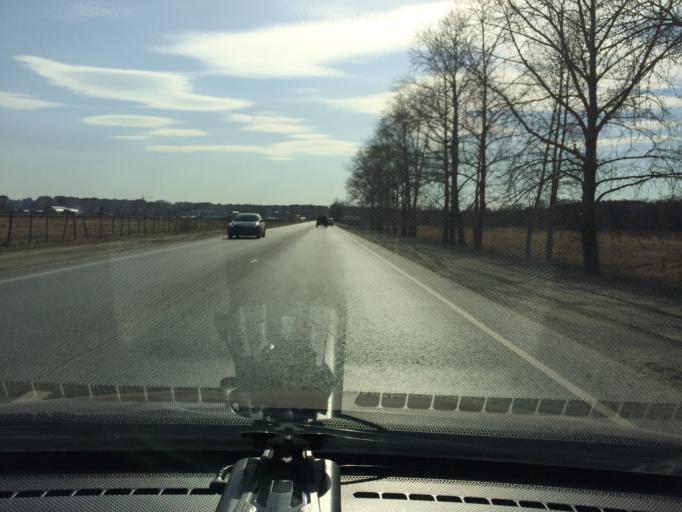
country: RU
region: Mariy-El
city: Yoshkar-Ola
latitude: 56.6496
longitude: 47.9444
